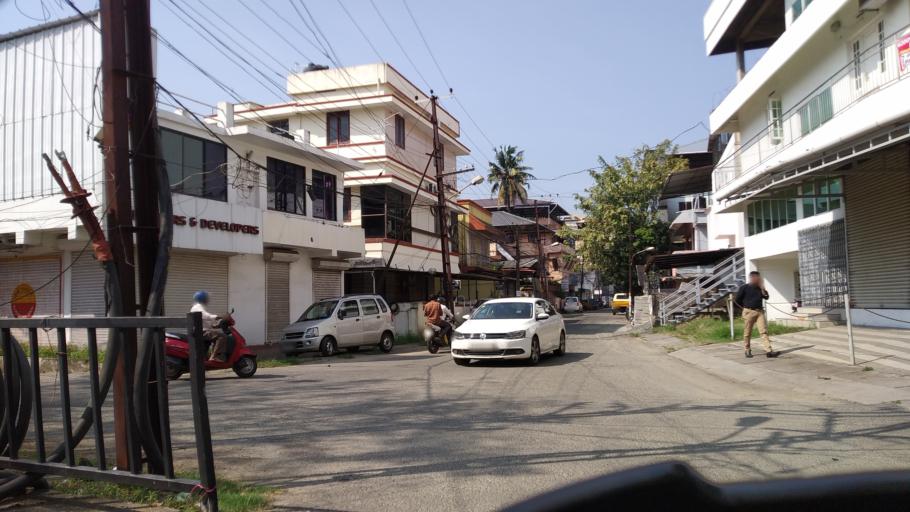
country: IN
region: Kerala
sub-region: Ernakulam
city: Cochin
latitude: 9.9615
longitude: 76.2924
